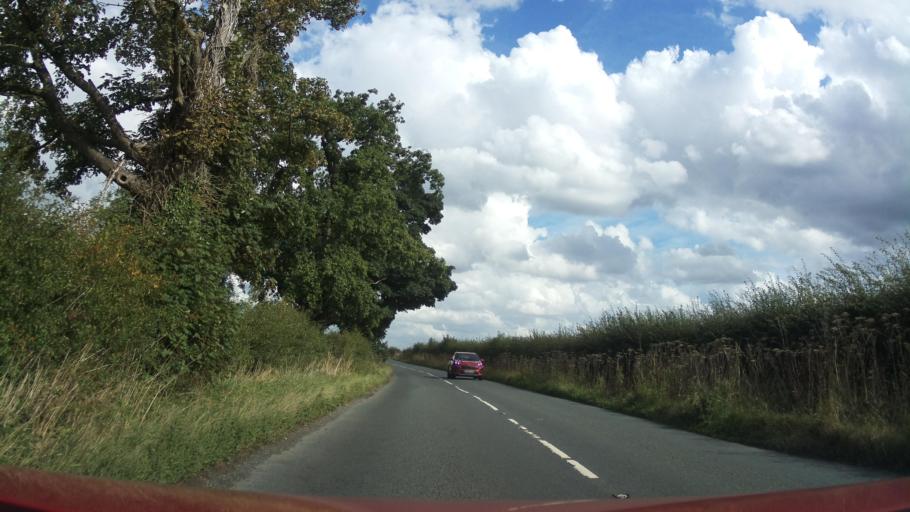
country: GB
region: England
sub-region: North Yorkshire
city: Bedale
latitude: 54.2093
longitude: -1.6137
